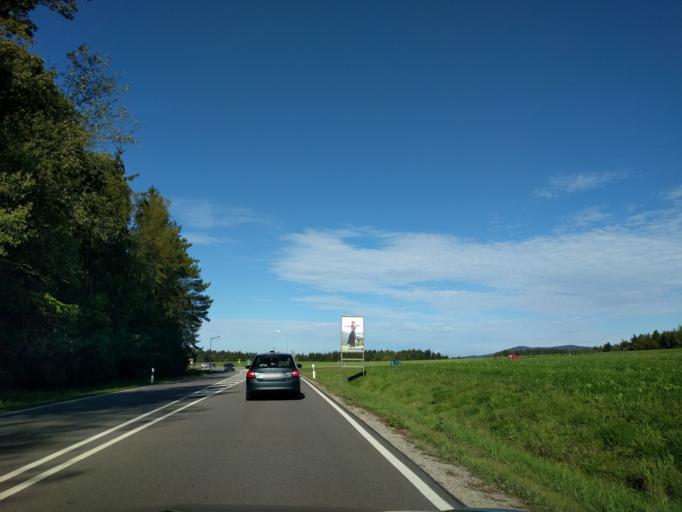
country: DE
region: Bavaria
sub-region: Lower Bavaria
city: Geiersthal
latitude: 49.0431
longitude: 12.9384
